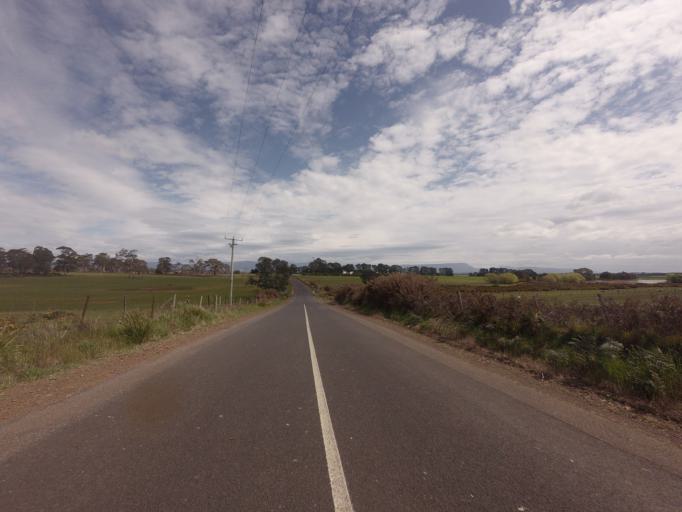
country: AU
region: Tasmania
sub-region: Northern Midlands
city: Longford
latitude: -41.7144
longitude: 147.1925
